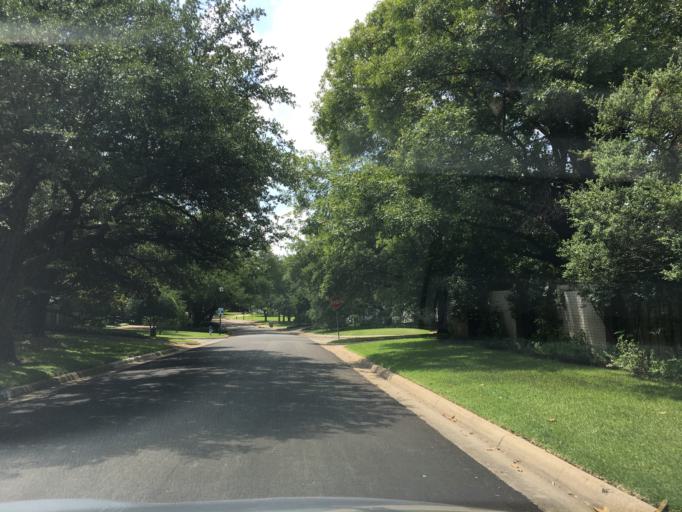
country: US
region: Texas
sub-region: Dallas County
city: University Park
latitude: 32.8729
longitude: -96.7800
